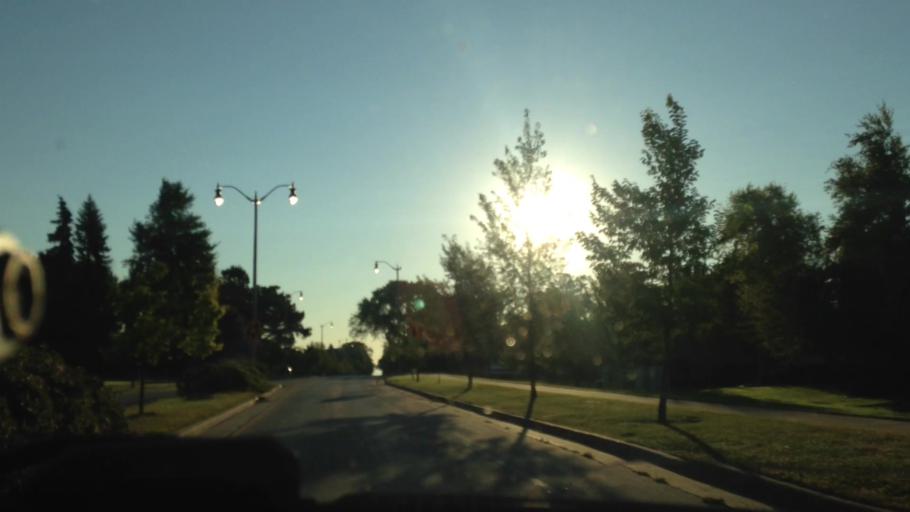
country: US
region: Wisconsin
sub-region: Ozaukee County
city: Port Washington
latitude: 43.3869
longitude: -87.8966
